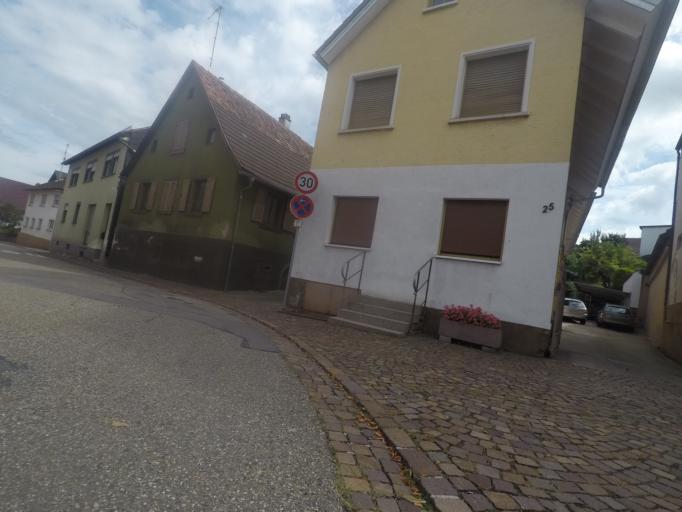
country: DE
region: Baden-Wuerttemberg
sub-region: Karlsruhe Region
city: Malsch
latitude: 48.8602
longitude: 8.3314
